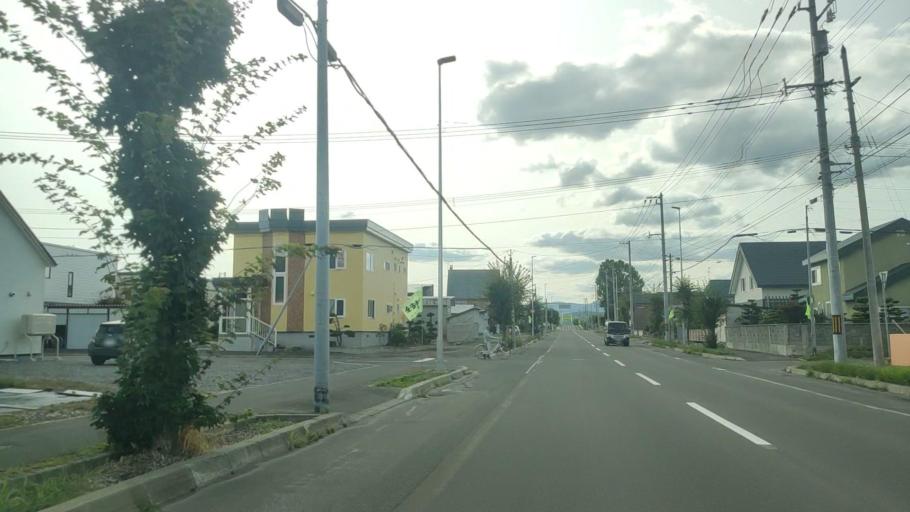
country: JP
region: Hokkaido
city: Nayoro
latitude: 44.3464
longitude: 142.4484
